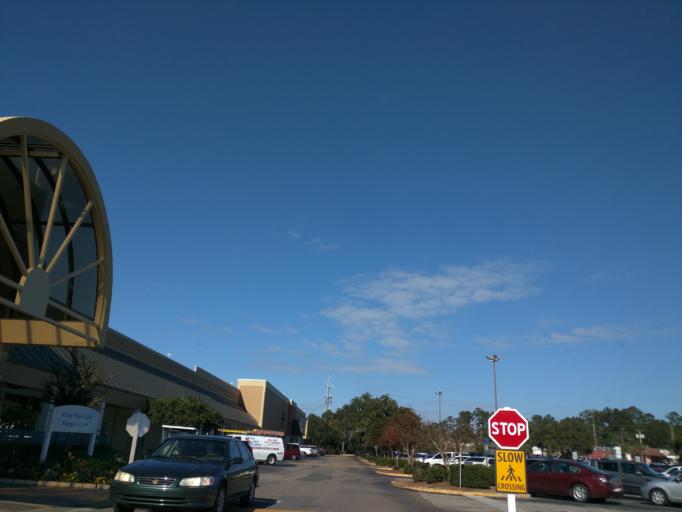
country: US
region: Florida
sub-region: Leon County
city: Tallahassee
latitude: 30.4659
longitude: -84.2869
